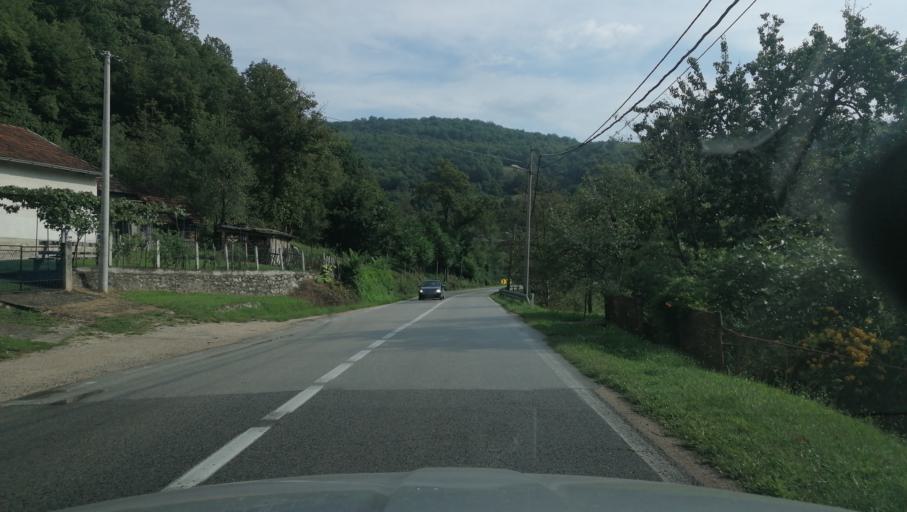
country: BA
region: Republika Srpska
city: Hiseti
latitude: 44.6743
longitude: 17.1464
